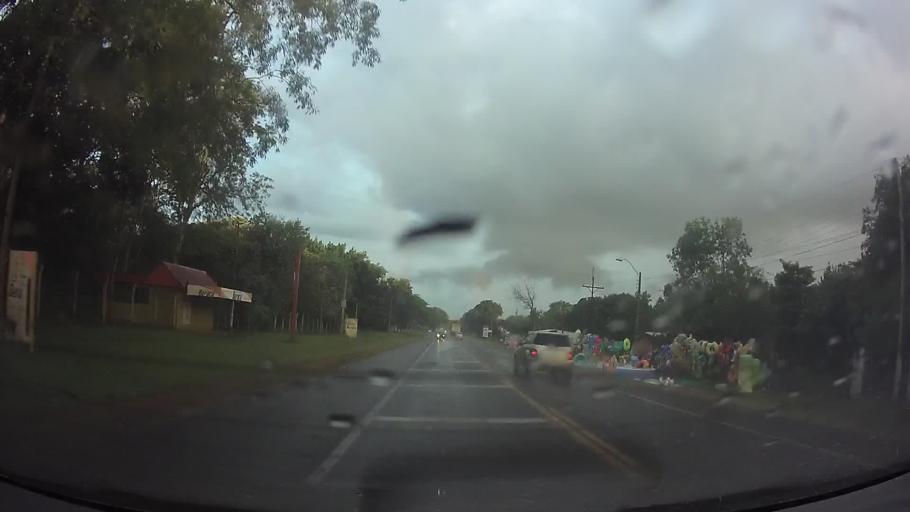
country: PY
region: Paraguari
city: Paraguari
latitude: -25.5986
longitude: -57.2034
